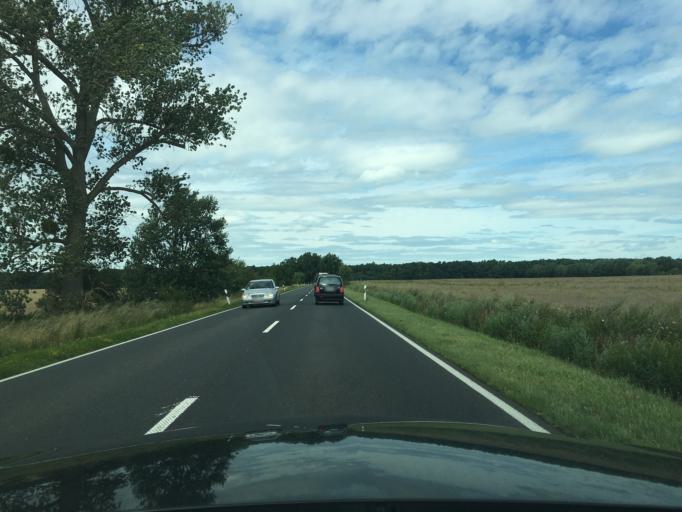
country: DE
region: Brandenburg
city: Gransee
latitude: 53.0504
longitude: 13.1942
